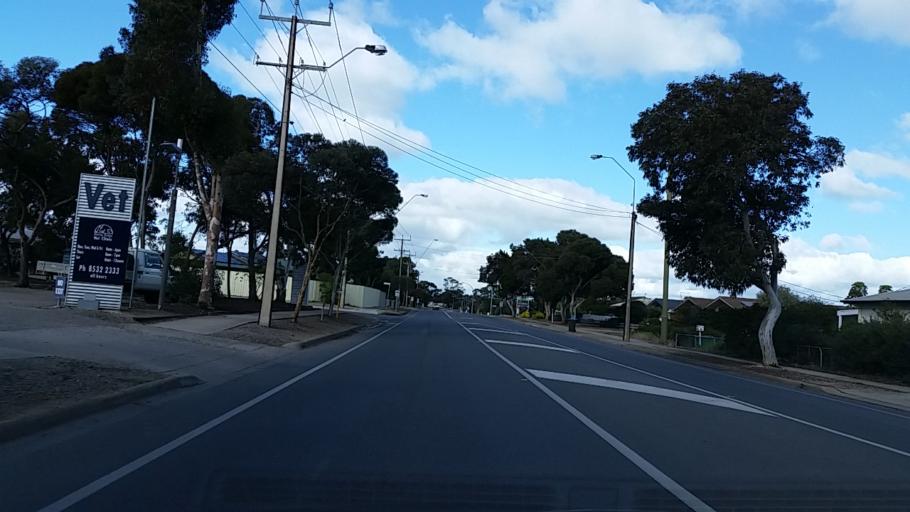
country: AU
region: South Australia
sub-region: Murray Bridge
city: Murray Bridge
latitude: -35.1334
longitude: 139.2811
